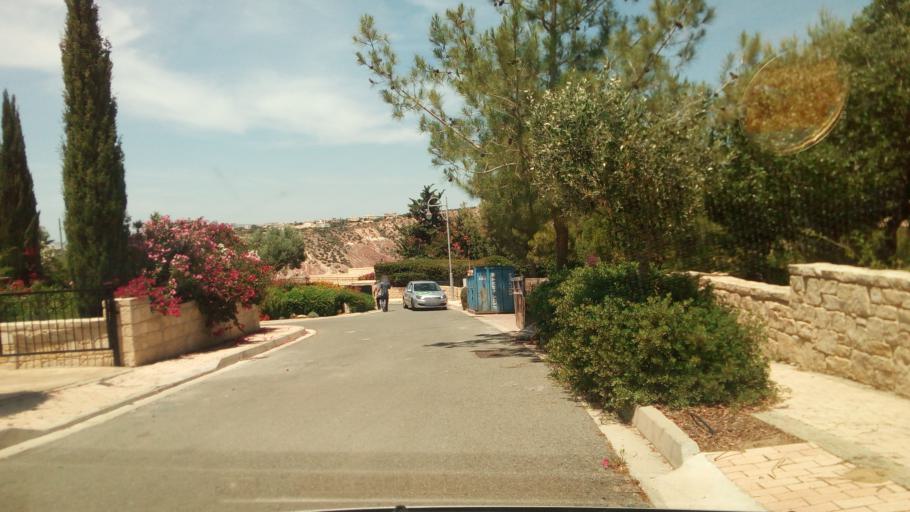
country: CY
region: Limassol
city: Pissouri
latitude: 34.6897
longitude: 32.6094
